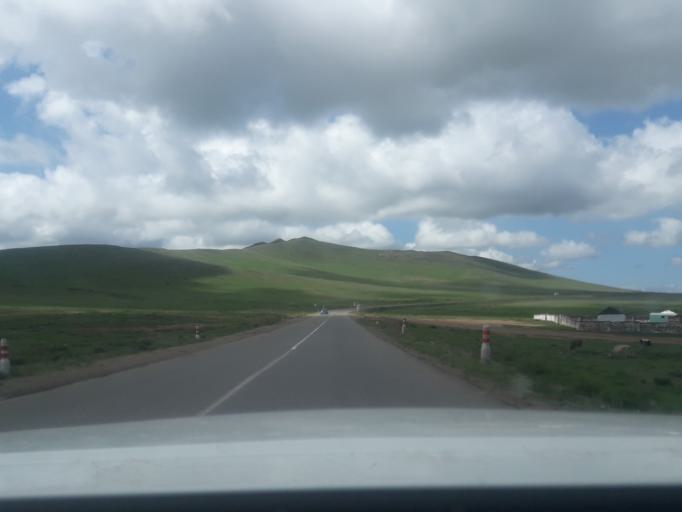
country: MN
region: Central Aimak
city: Altanbulag
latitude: 47.8996
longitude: 106.4247
